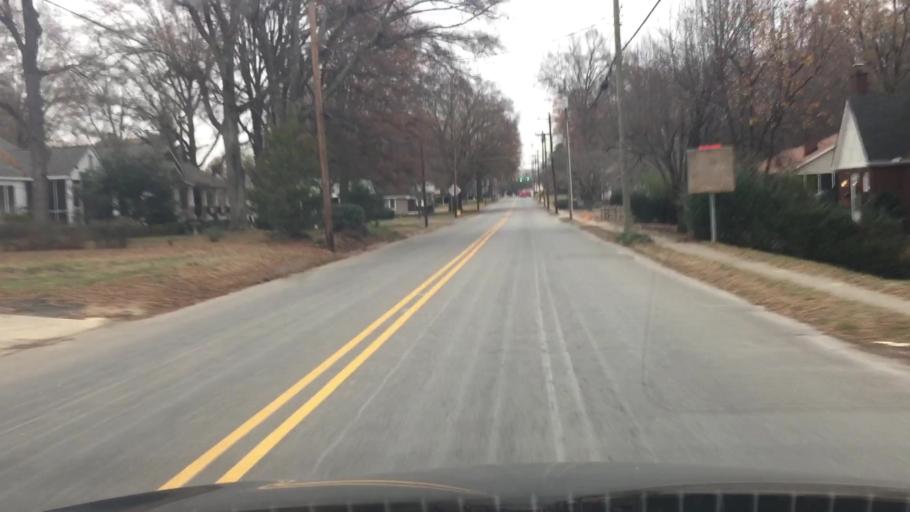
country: US
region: North Carolina
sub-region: Iredell County
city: Mooresville
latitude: 35.5826
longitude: -80.8024
